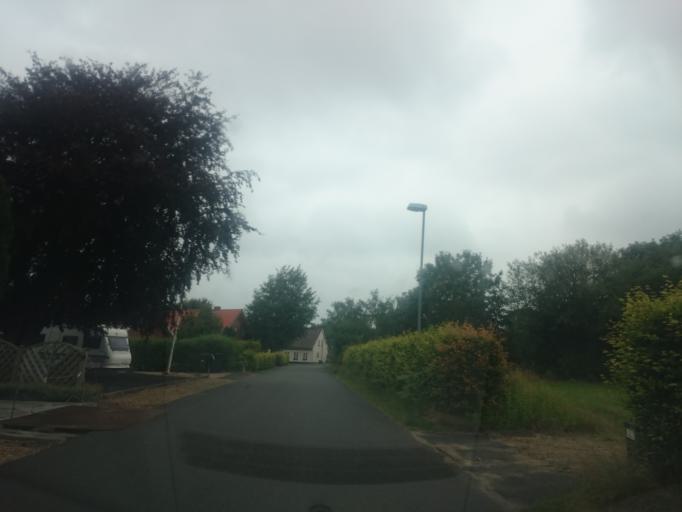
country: DK
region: South Denmark
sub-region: Vejen Kommune
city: Holsted
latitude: 55.5964
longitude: 8.8017
